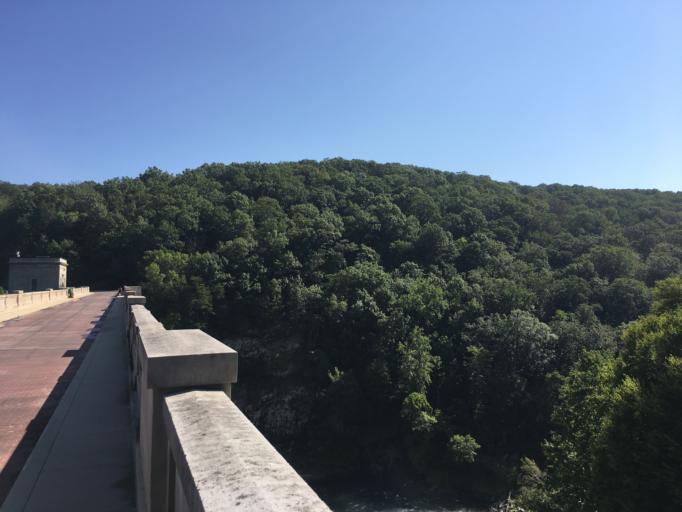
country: US
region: Pennsylvania
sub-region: York County
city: New Freedom
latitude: 39.6190
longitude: -76.7081
